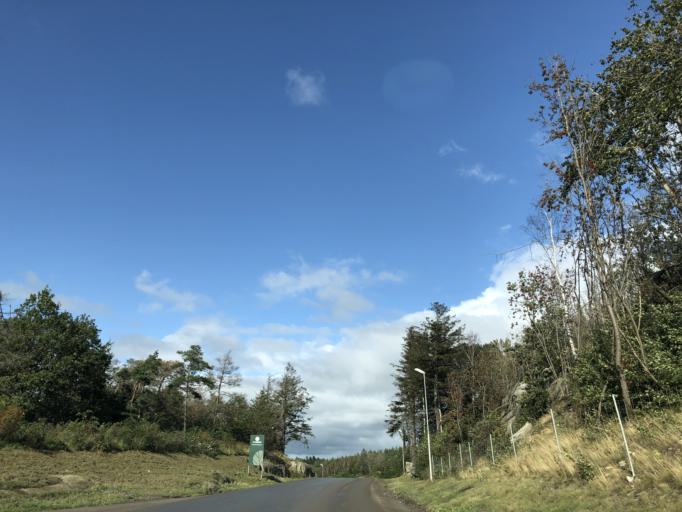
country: SE
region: Vaestra Goetaland
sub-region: Goteborg
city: Majorna
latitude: 57.7126
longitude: 11.8506
